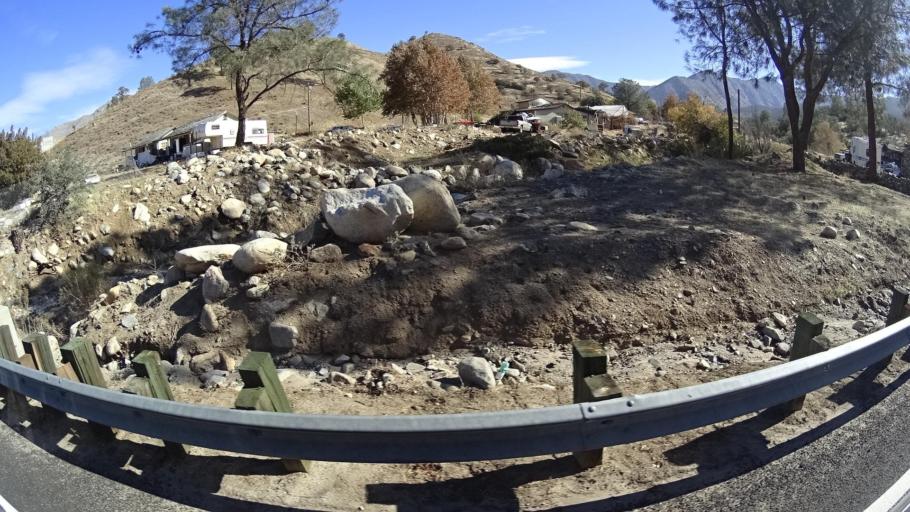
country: US
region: California
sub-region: Kern County
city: Bodfish
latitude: 35.5959
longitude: -118.4919
